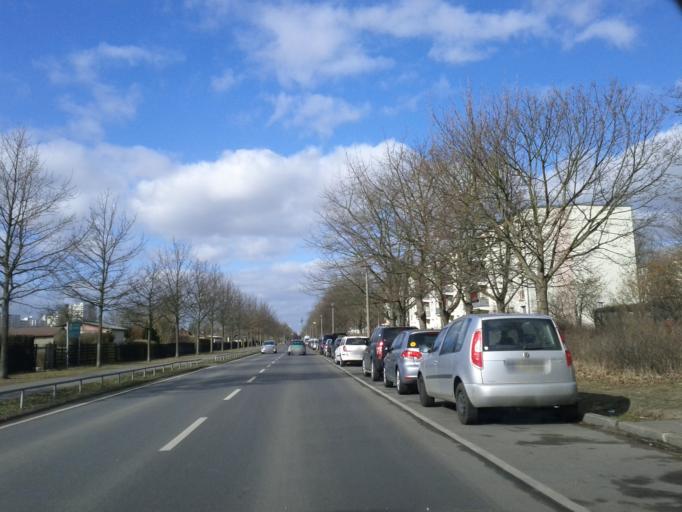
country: DE
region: Berlin
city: Plaenterwald
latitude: 52.4725
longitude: 13.4774
